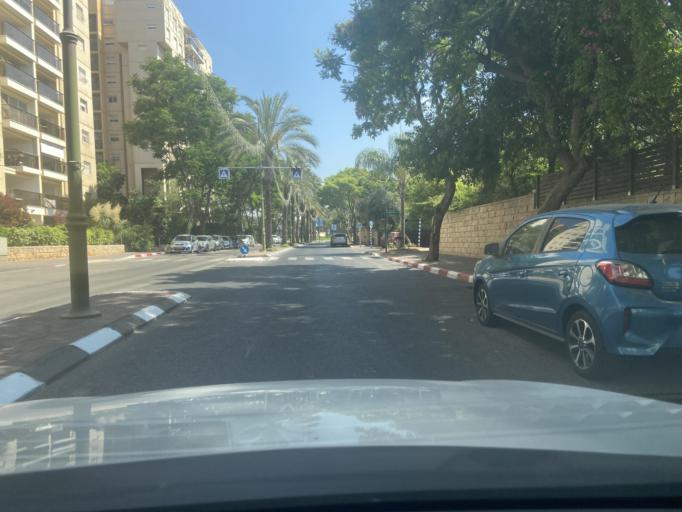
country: IL
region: Central District
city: Yehud
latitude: 32.0337
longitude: 34.8810
